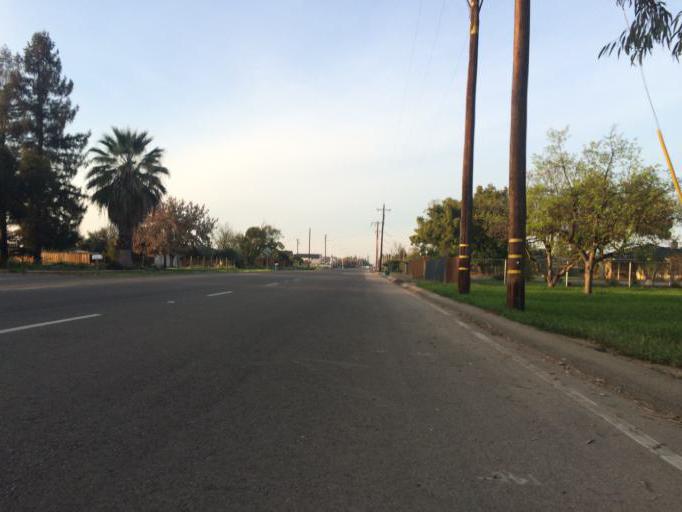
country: US
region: California
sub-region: Fresno County
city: Tarpey Village
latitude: 36.7871
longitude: -119.6730
